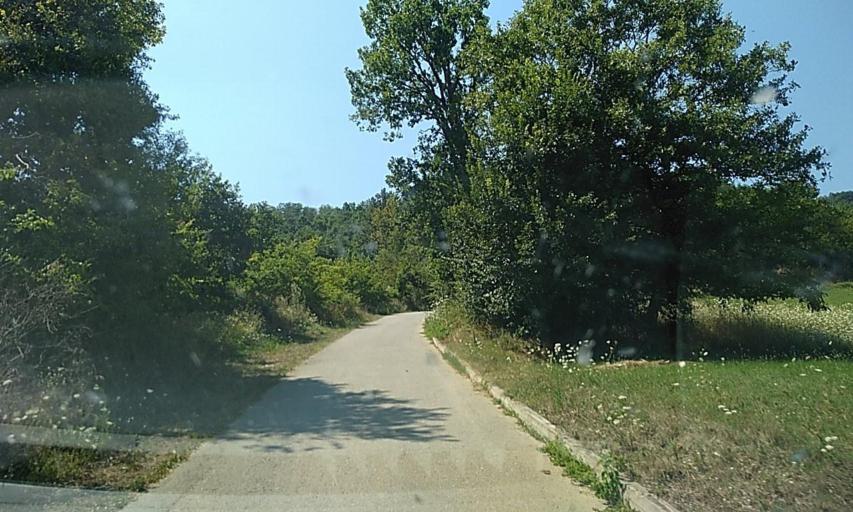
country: RS
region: Central Serbia
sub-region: Pcinjski Okrug
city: Vladicin Han
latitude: 42.7535
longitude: 22.0758
